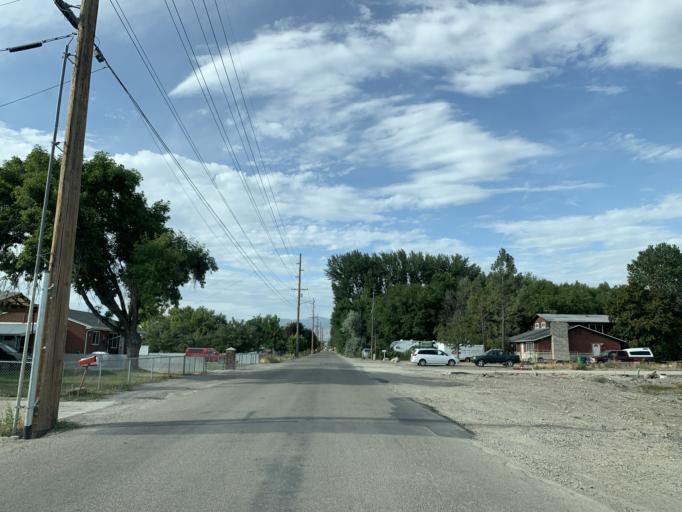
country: US
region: Utah
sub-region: Utah County
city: Provo
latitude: 40.2216
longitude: -111.6873
